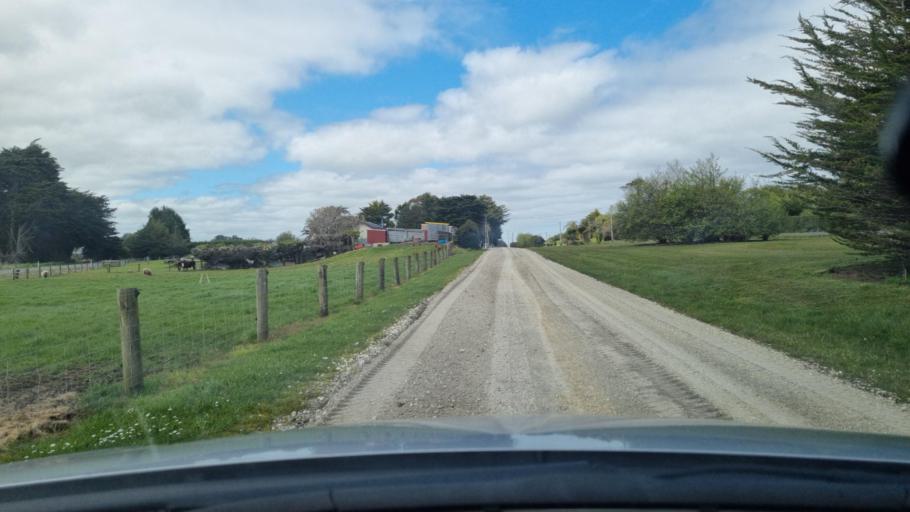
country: NZ
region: Southland
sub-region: Invercargill City
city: Invercargill
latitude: -46.4397
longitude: 168.3847
